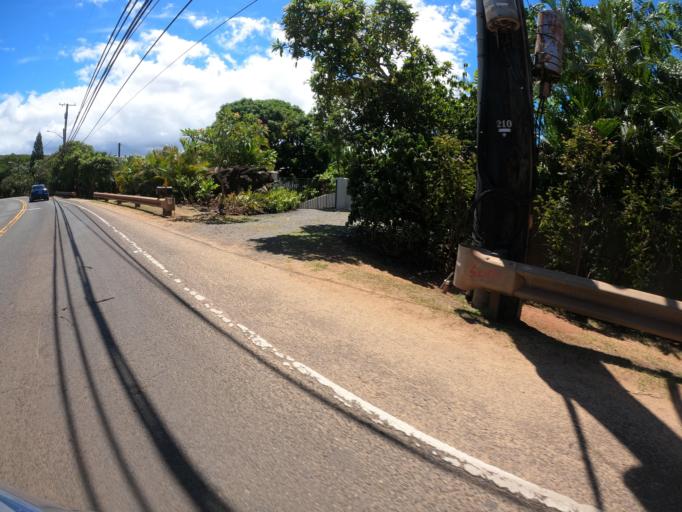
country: US
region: Hawaii
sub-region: Honolulu County
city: Pupukea
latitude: 21.6441
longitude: -158.0639
